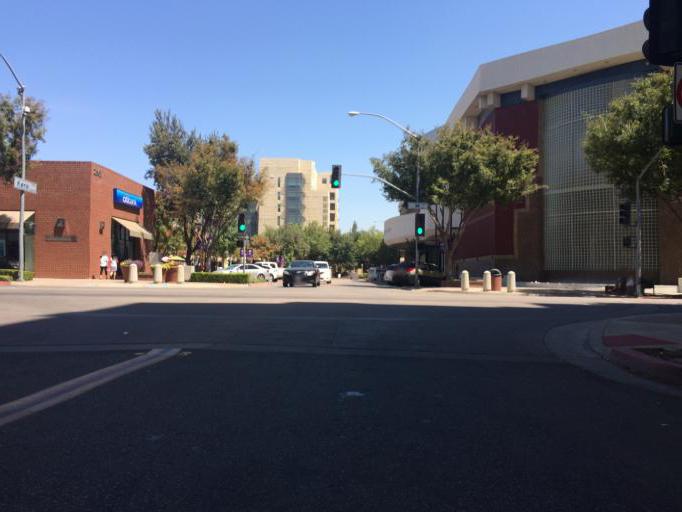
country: US
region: California
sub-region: Fresno County
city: Fresno
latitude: 36.7349
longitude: -119.7862
